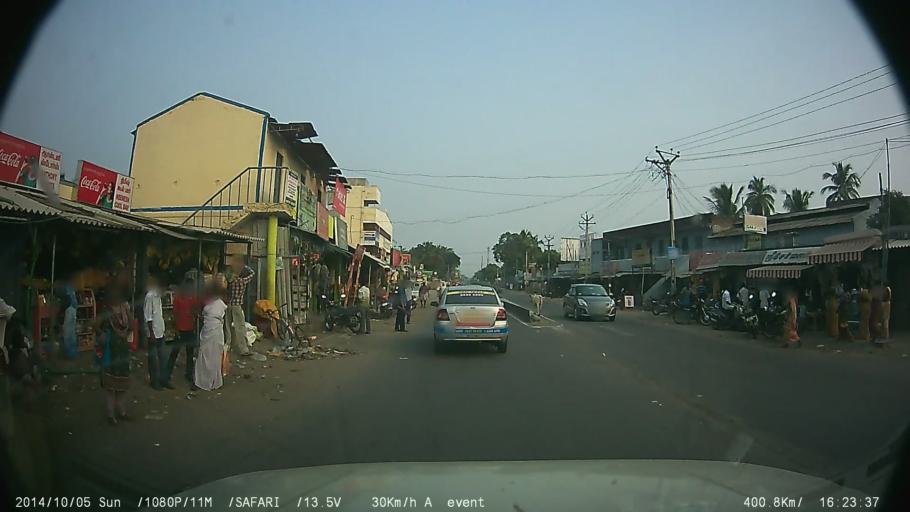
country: IN
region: Tamil Nadu
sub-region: Kancheepuram
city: Vengavasal
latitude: 12.8276
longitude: 80.1651
